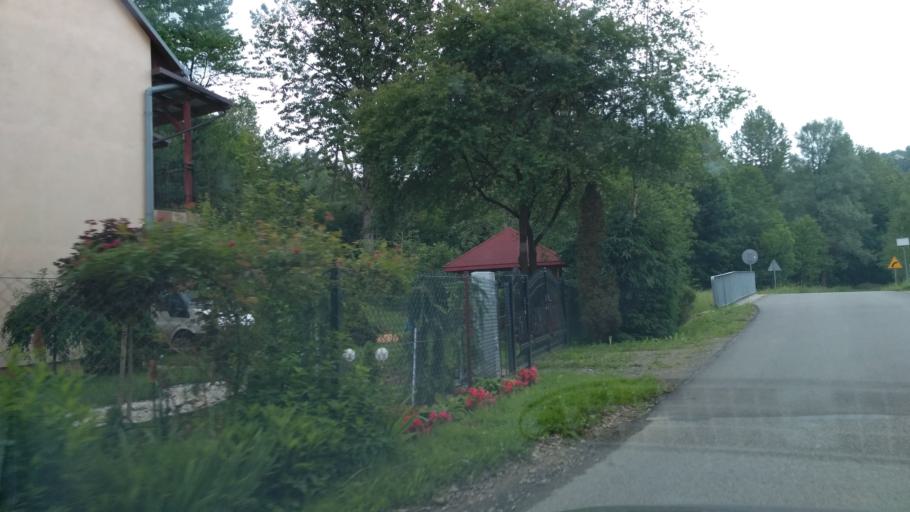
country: PL
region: Subcarpathian Voivodeship
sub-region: Powiat przemyski
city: Nienadowa
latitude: 49.8442
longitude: 22.4136
